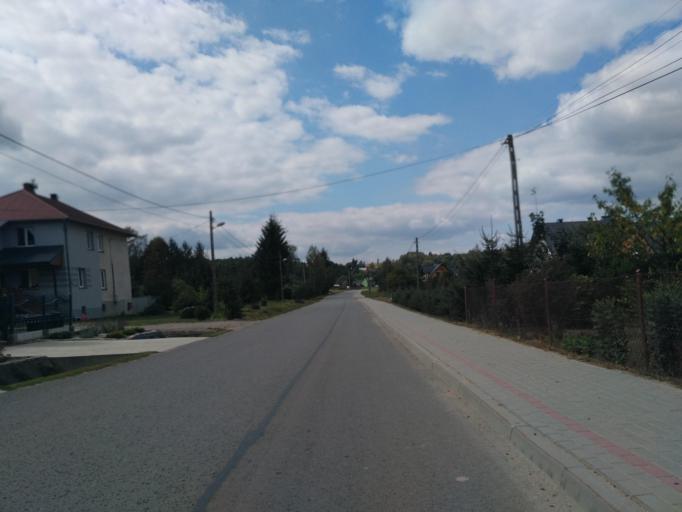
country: PL
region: Subcarpathian Voivodeship
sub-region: Powiat rzeszowski
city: Dynow
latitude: 49.8148
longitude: 22.2827
